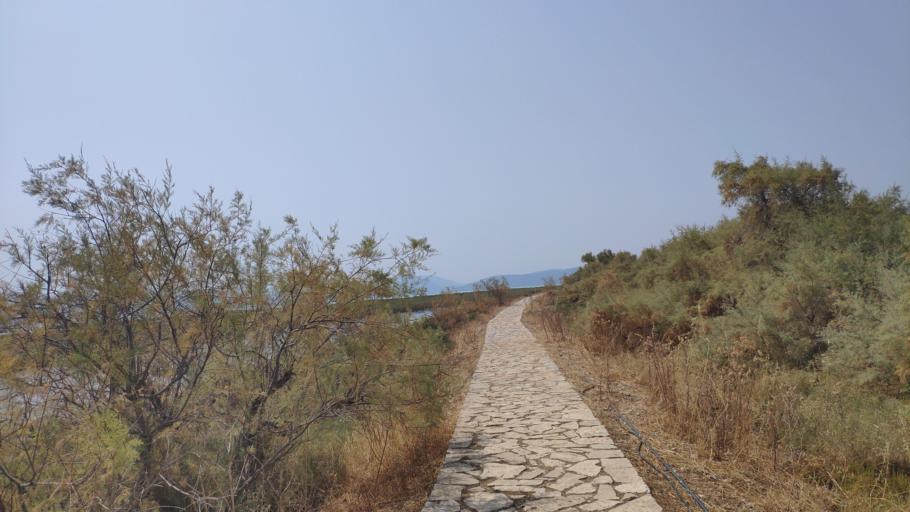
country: GR
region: West Greece
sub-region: Nomos Aitolias kai Akarnanias
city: Menidi
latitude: 39.0326
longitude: 21.0748
